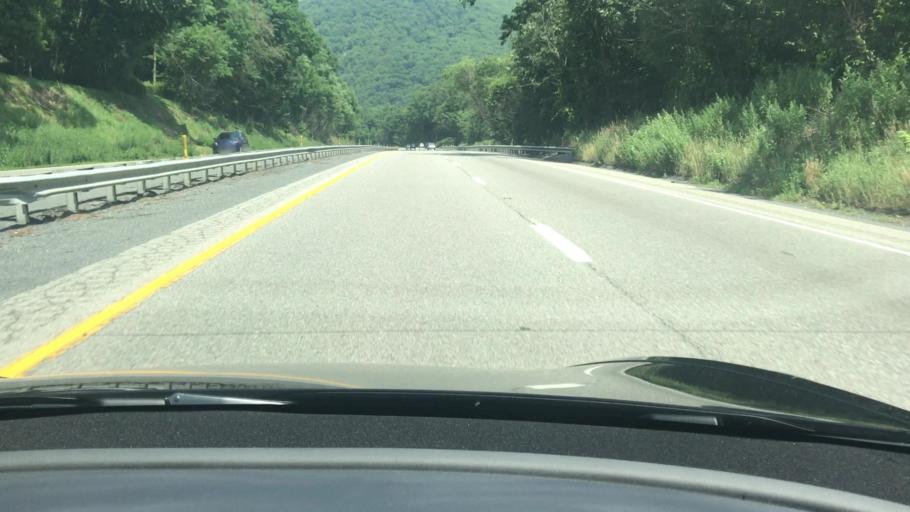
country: US
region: Pennsylvania
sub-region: Mifflin County
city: Yeagertown
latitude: 40.6438
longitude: -77.5841
